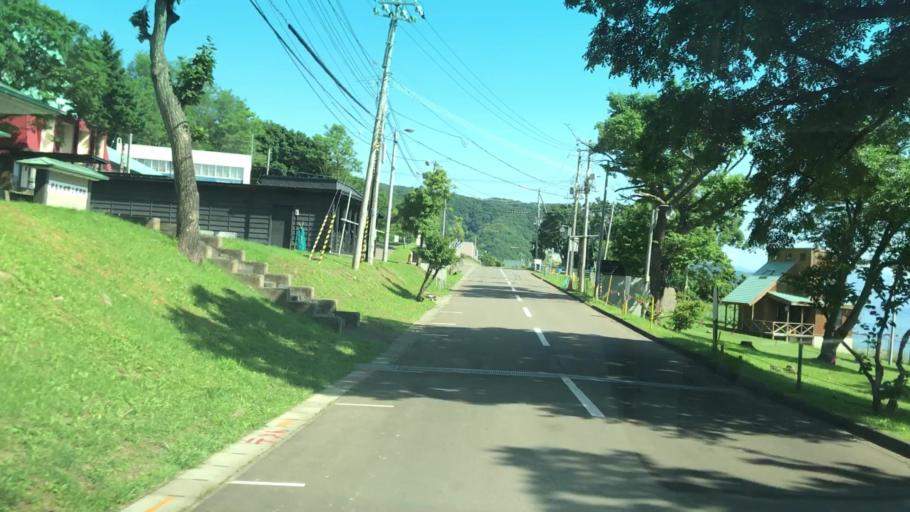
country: JP
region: Hokkaido
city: Iwanai
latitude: 43.1484
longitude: 140.4200
